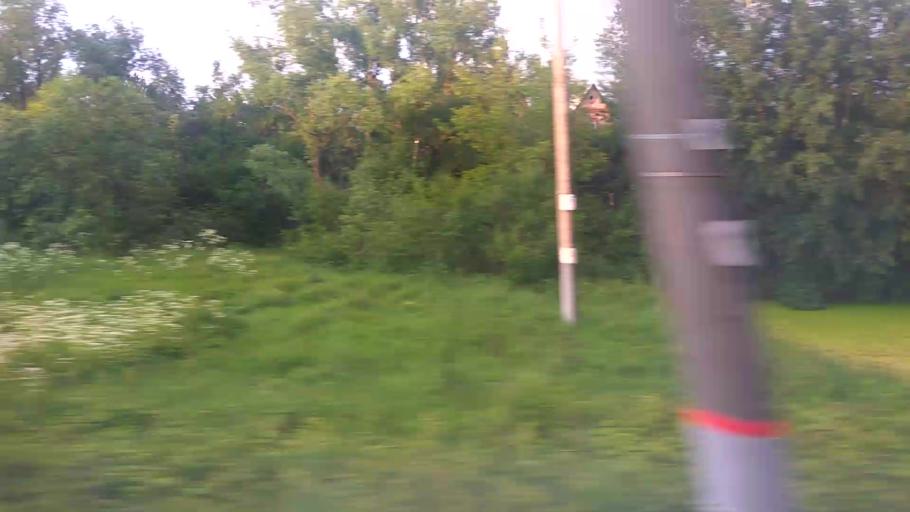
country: RU
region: Moskovskaya
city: Stupino
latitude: 54.8975
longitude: 38.0910
